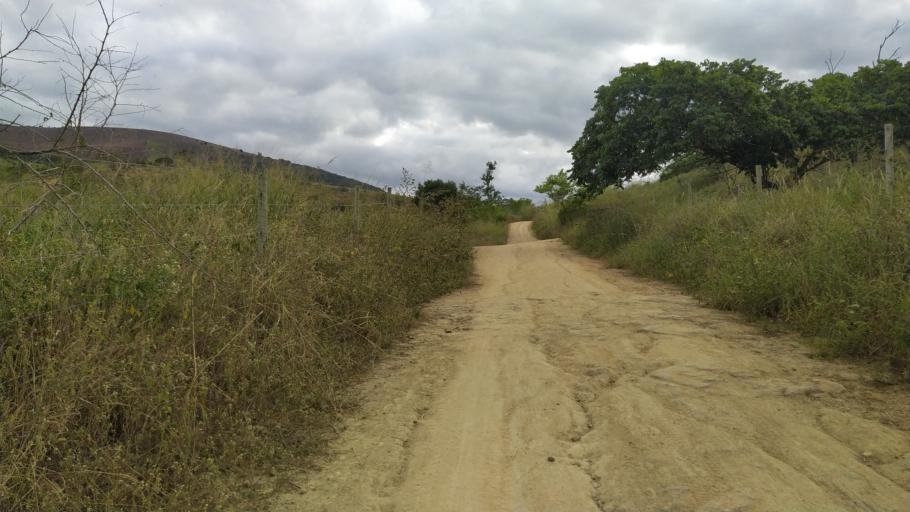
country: BR
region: Minas Gerais
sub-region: Almenara
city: Almenara
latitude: -16.6301
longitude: -40.4603
